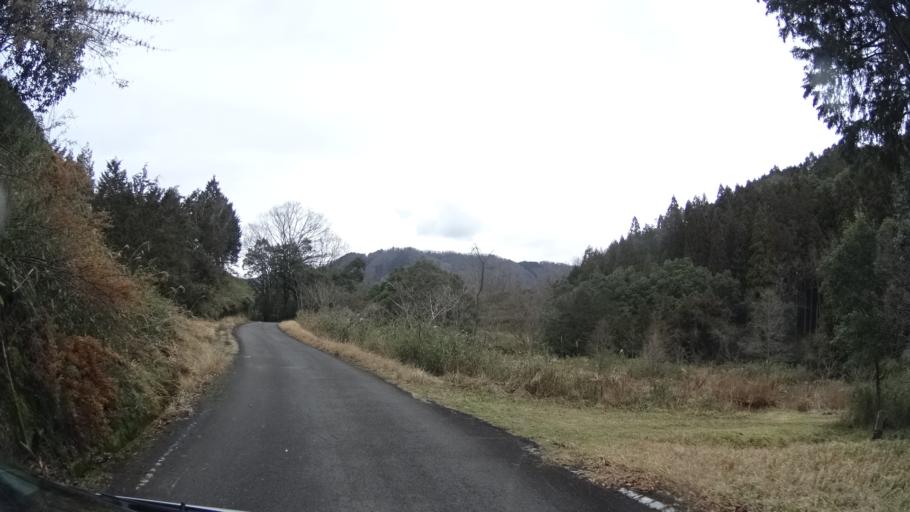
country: JP
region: Kyoto
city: Ayabe
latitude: 35.3189
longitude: 135.3618
